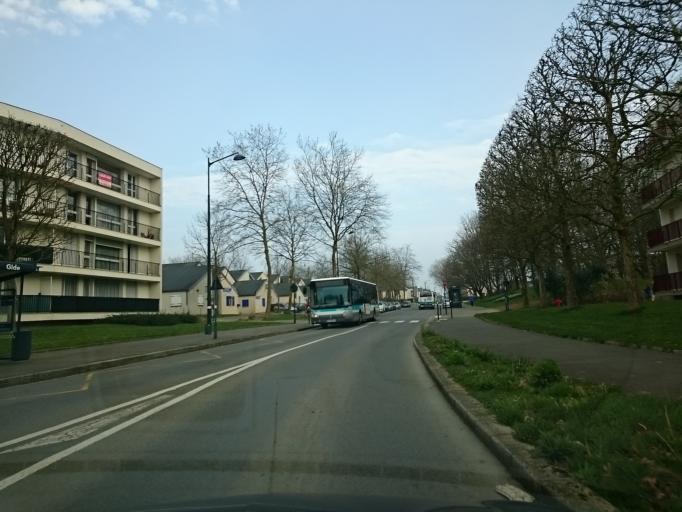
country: FR
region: Brittany
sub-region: Departement d'Ille-et-Vilaine
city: Rennes
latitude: 48.0919
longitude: -1.6583
